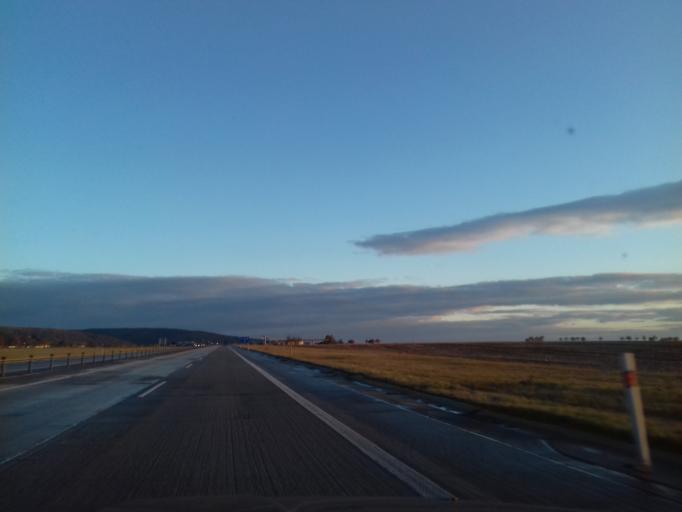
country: CZ
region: South Moravian
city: Pustimer
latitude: 49.3013
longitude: 17.0276
